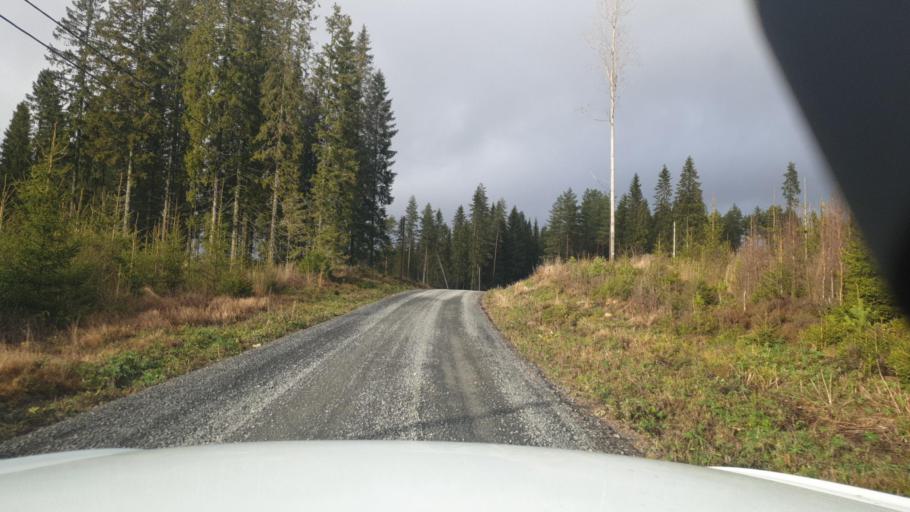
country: SE
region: Vaermland
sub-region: Eda Kommun
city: Charlottenberg
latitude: 60.1468
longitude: 12.5961
